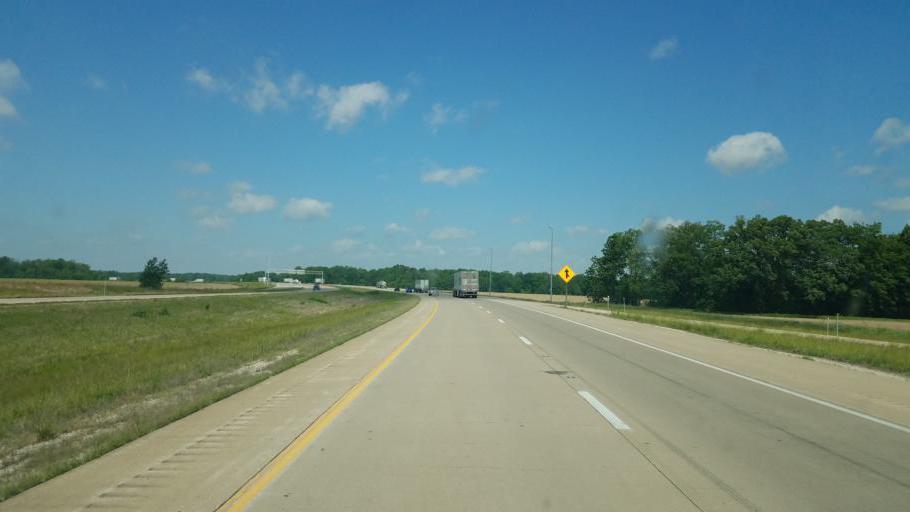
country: US
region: Indiana
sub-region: Vigo County
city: West Terre Haute
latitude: 39.4284
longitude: -87.5615
